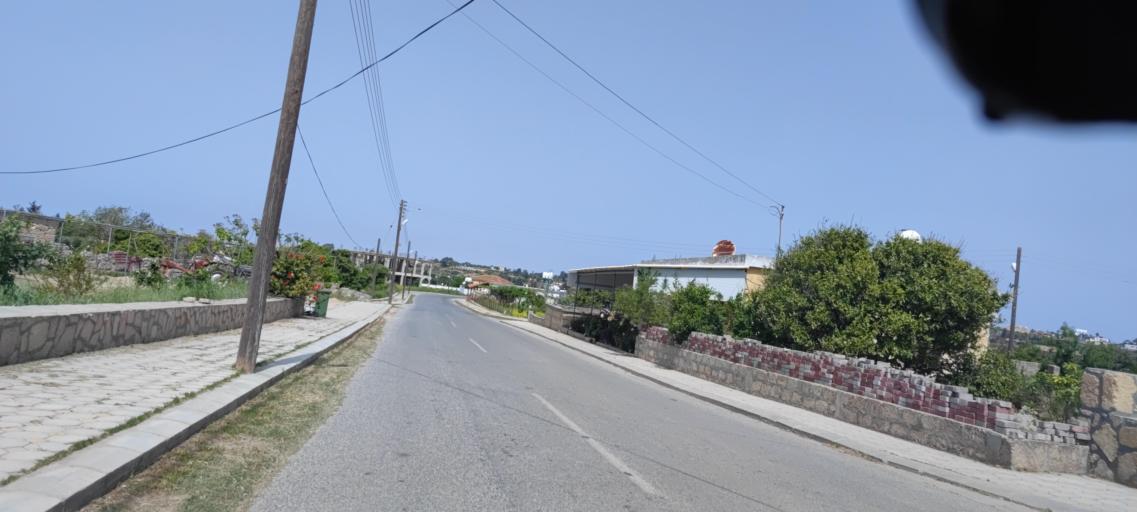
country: CY
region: Ammochostos
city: Rizokarpaso
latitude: 35.5918
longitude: 34.3868
